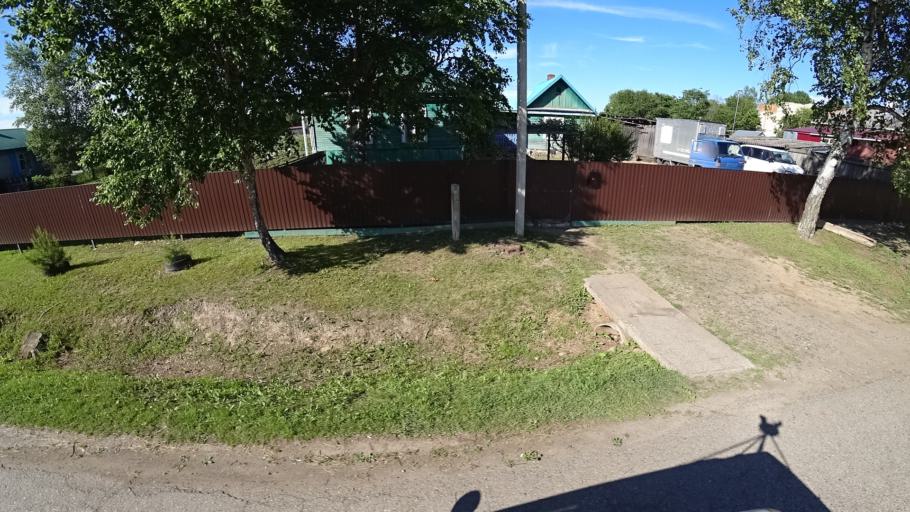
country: RU
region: Khabarovsk Krai
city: Khor
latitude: 47.8863
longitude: 134.9951
